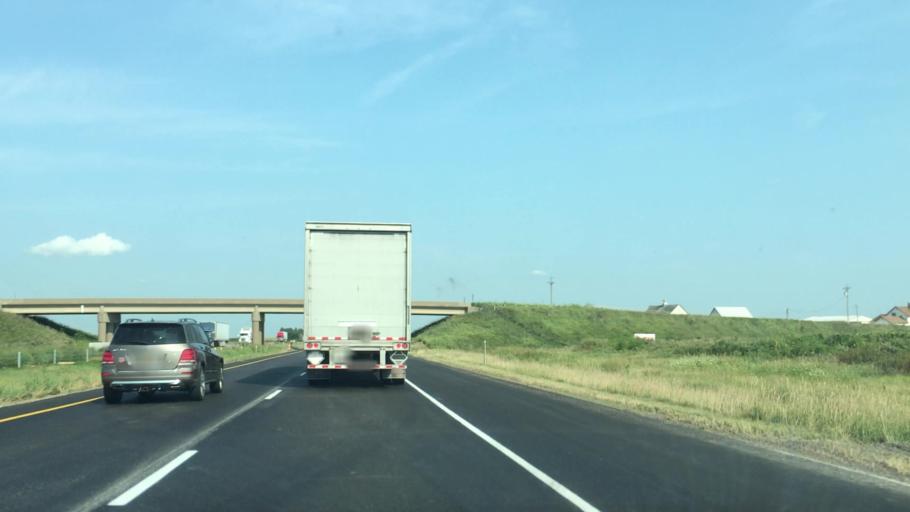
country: US
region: Iowa
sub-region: Scott County
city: Walcott
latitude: 41.6088
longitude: -90.7454
